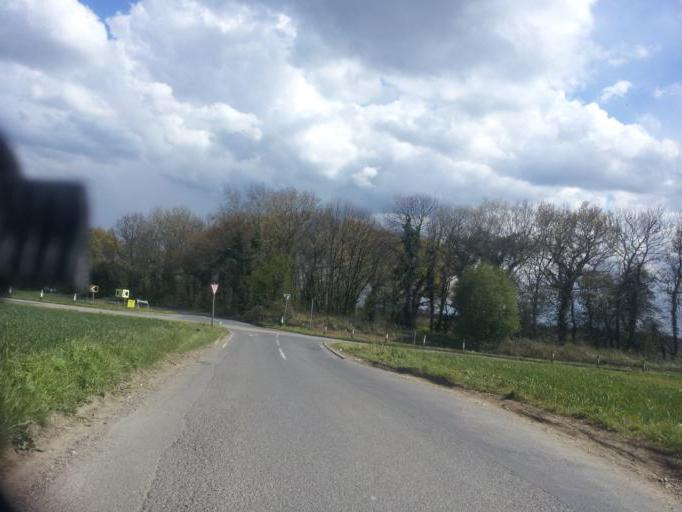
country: GB
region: England
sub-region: Kent
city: Boxley
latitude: 51.3223
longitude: 0.5584
